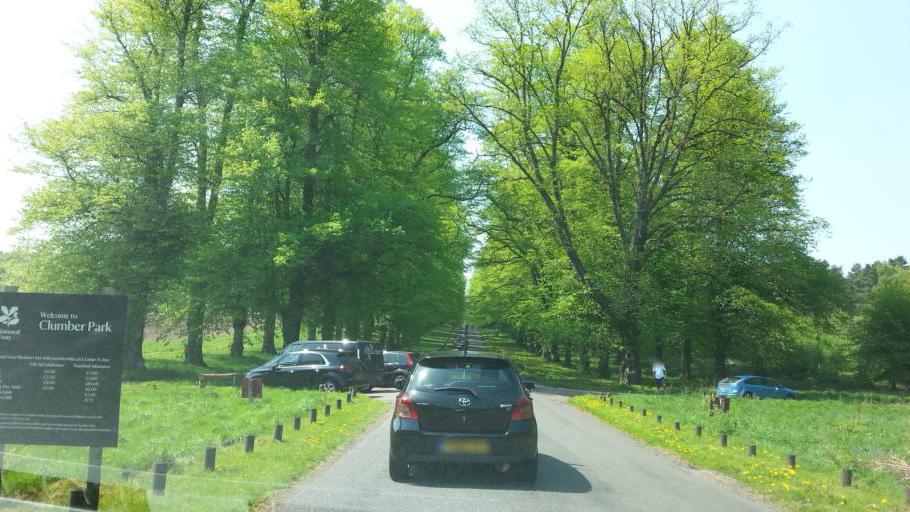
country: GB
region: England
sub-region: Nottinghamshire
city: Babworth
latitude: 53.2882
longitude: -1.0398
